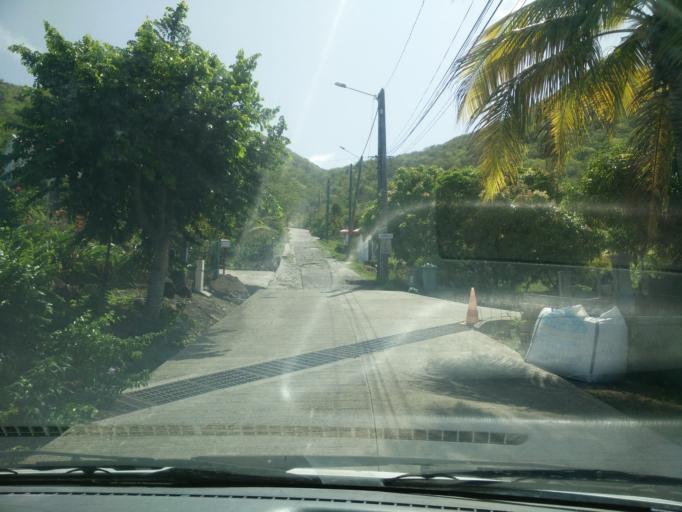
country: GP
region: Guadeloupe
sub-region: Guadeloupe
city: Terre-de-Bas
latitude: 15.8561
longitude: -61.6260
